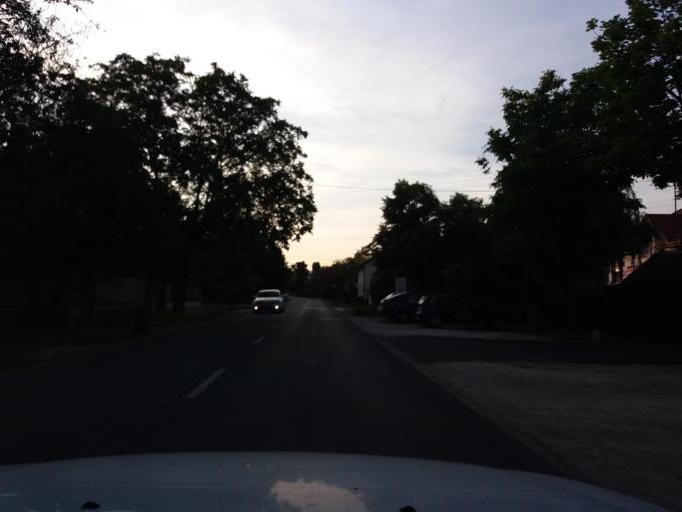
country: HU
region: Budapest
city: Budapest XXII. keruelet
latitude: 47.4458
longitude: 19.0279
